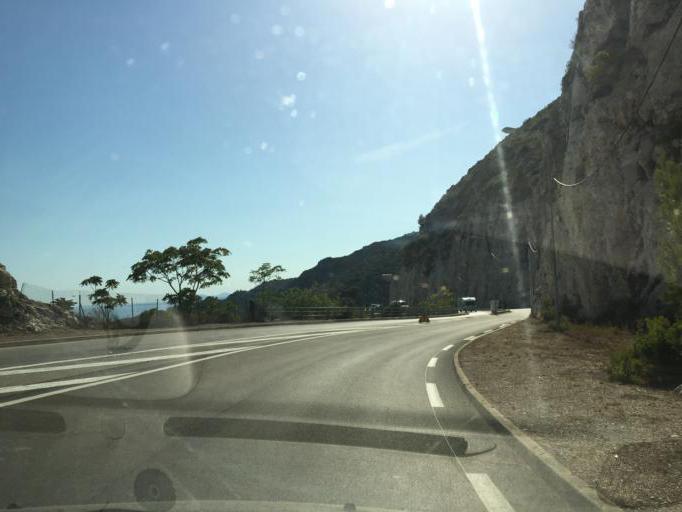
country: FR
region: Provence-Alpes-Cote d'Azur
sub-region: Departement des Alpes-Maritimes
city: Eze
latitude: 43.7281
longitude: 7.3566
